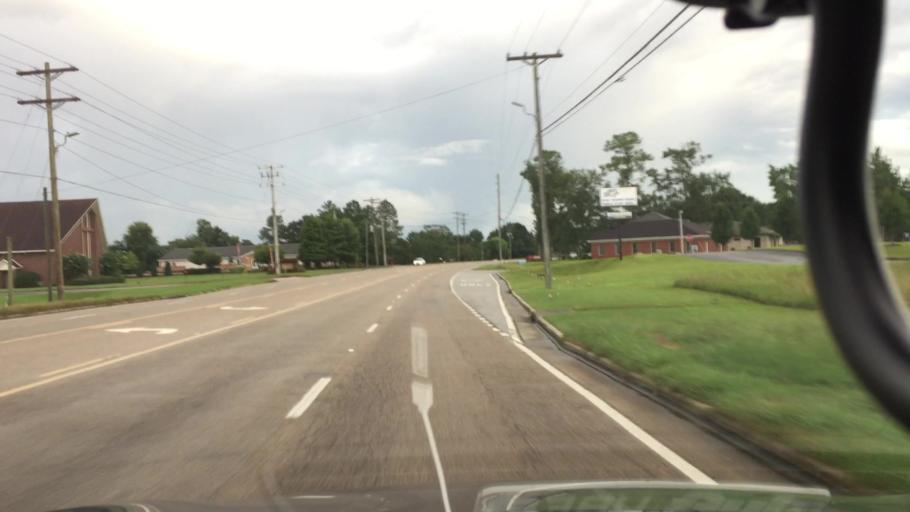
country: US
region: Alabama
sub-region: Pike County
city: Troy
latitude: 31.7774
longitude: -85.9622
